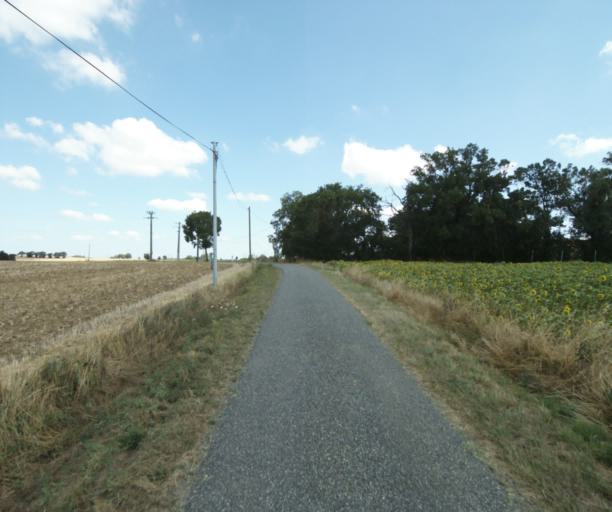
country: FR
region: Midi-Pyrenees
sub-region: Departement de la Haute-Garonne
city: Auriac-sur-Vendinelle
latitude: 43.4582
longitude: 1.8050
